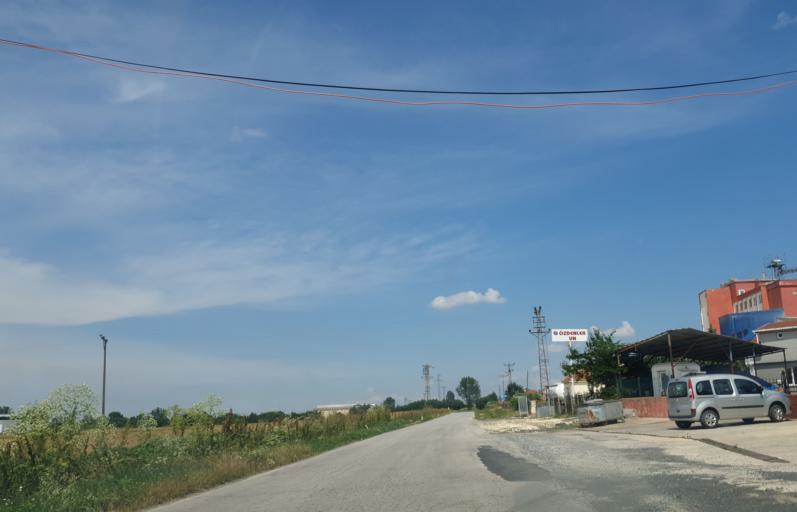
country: TR
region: Tekirdag
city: Muratli
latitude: 41.2037
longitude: 27.5216
